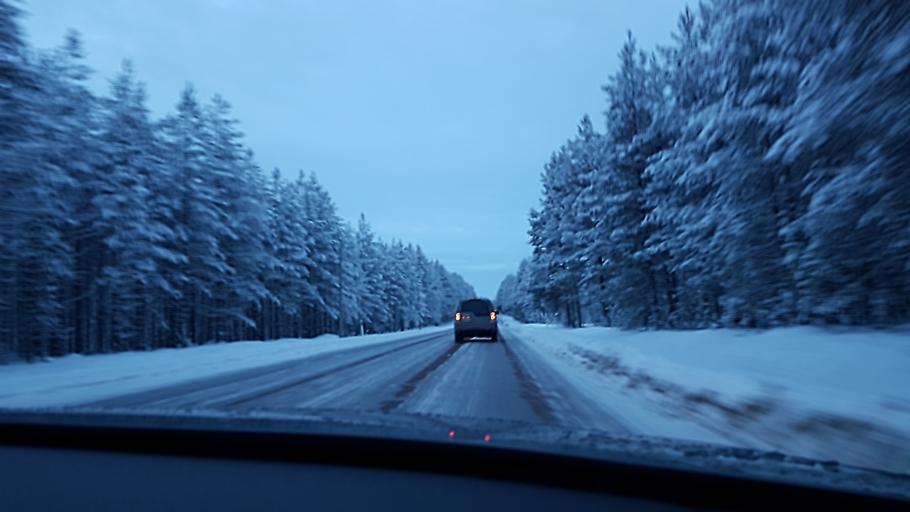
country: SE
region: Jaemtland
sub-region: Harjedalens Kommun
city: Sveg
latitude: 62.0514
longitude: 14.6257
